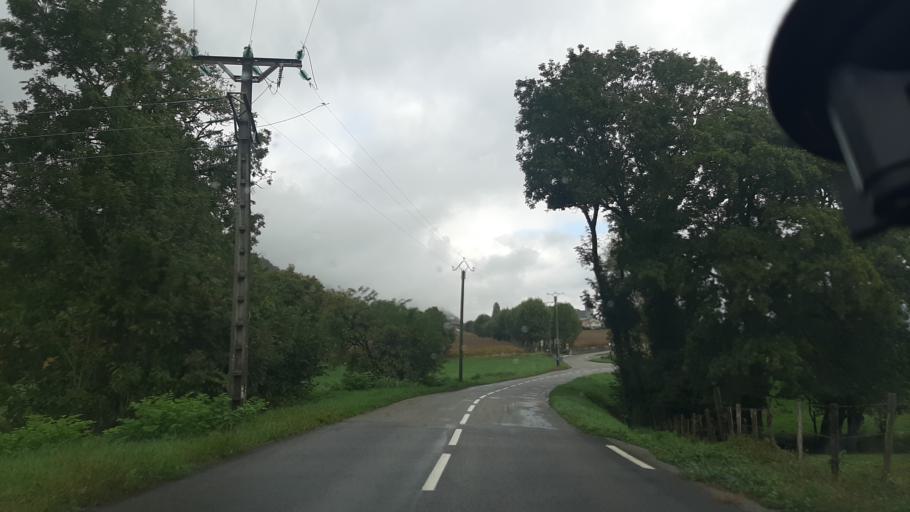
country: FR
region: Rhone-Alpes
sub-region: Departement de la Savoie
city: Gresy-sur-Isere
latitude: 45.6122
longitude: 6.2746
